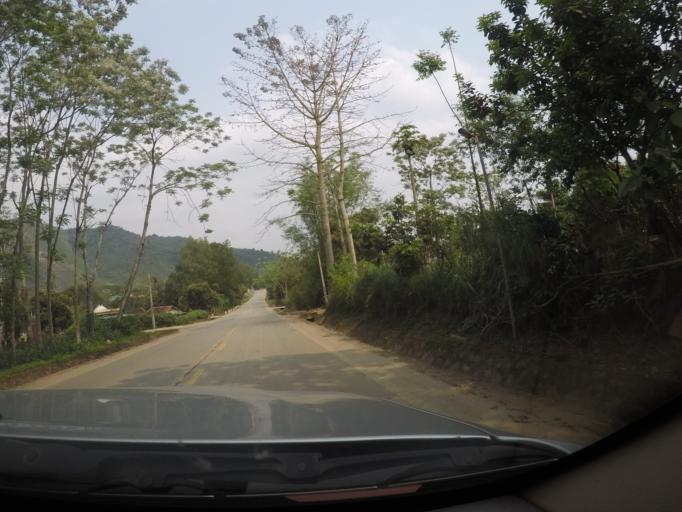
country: VN
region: Thanh Hoa
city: Thi Tran Yen Cat
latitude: 19.4782
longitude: 105.4074
